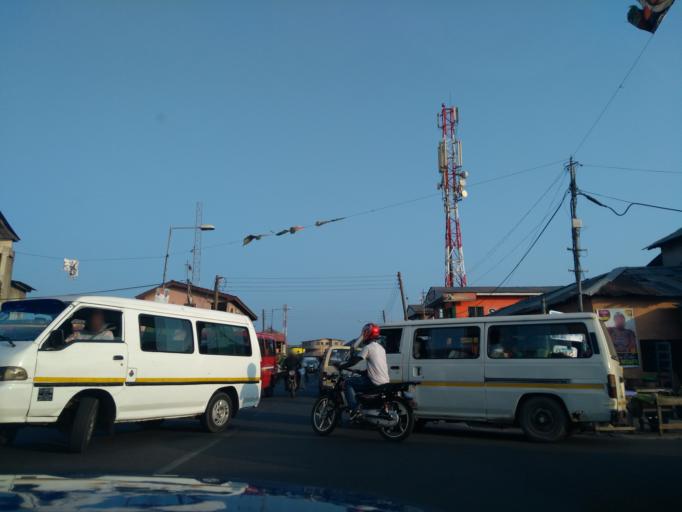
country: GH
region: Greater Accra
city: Accra
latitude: 5.5391
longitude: -0.2132
